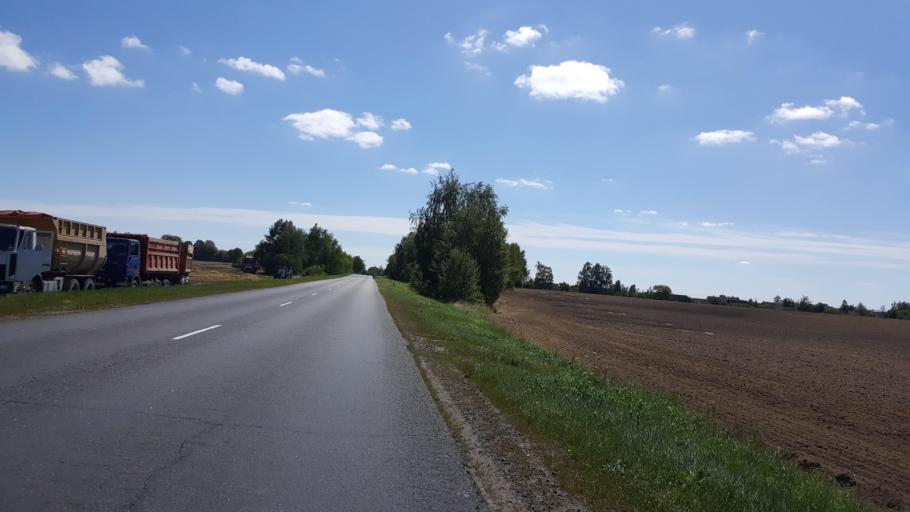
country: BY
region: Brest
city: Kobryn
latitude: 52.3494
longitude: 24.1963
